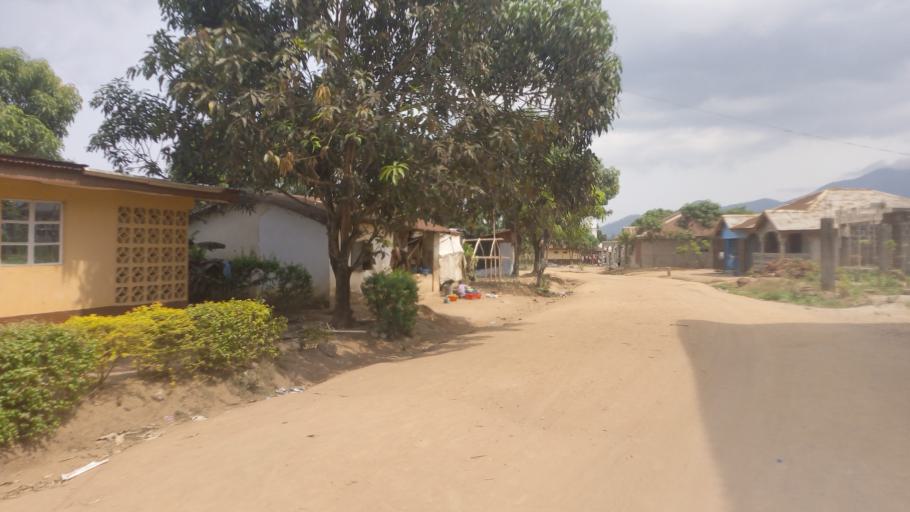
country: SL
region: Western Area
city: Waterloo
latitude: 8.3132
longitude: -13.0653
